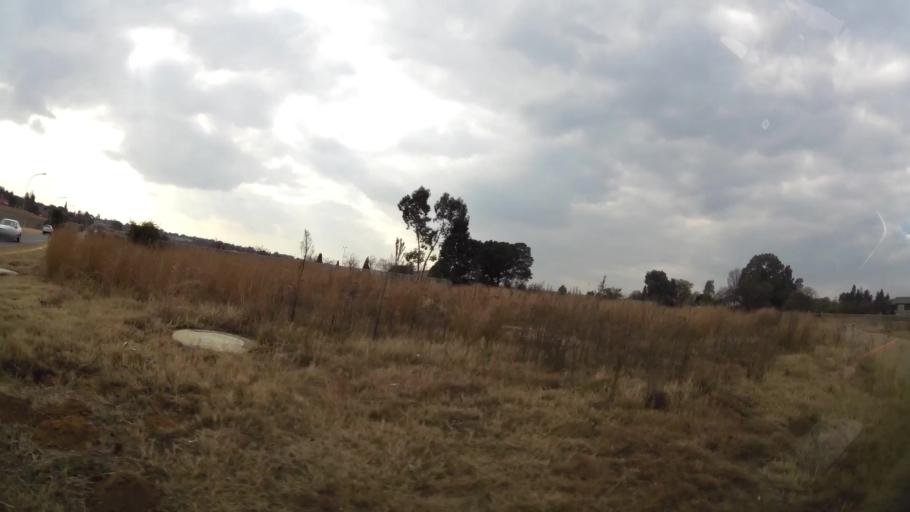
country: ZA
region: Gauteng
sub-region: Ekurhuleni Metropolitan Municipality
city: Benoni
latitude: -26.1417
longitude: 28.3558
